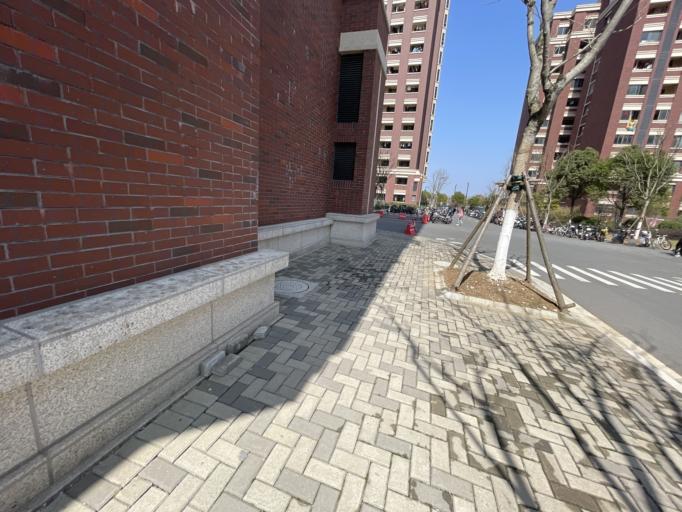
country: CN
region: Shanghai Shi
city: Shuyuan
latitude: 30.8959
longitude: 121.8855
